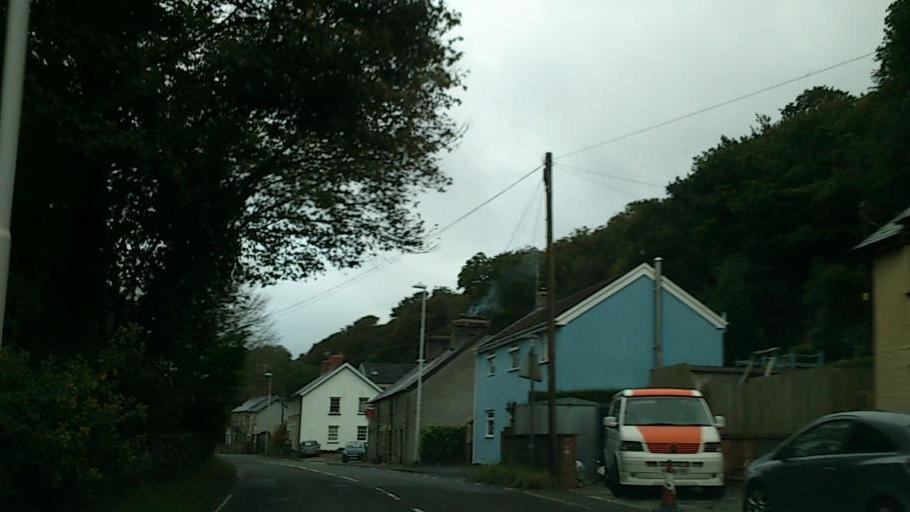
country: GB
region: Wales
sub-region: Sir Powys
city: Machynlleth
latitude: 52.5423
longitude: -3.9381
